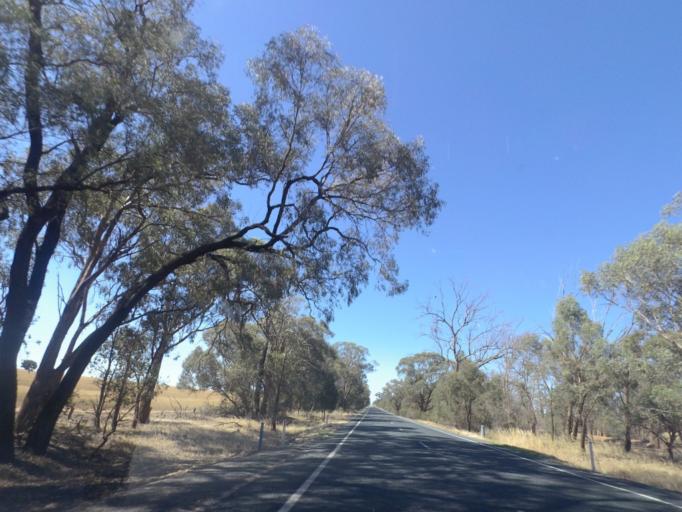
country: AU
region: New South Wales
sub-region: Bland
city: West Wyalong
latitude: -34.1495
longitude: 147.1187
